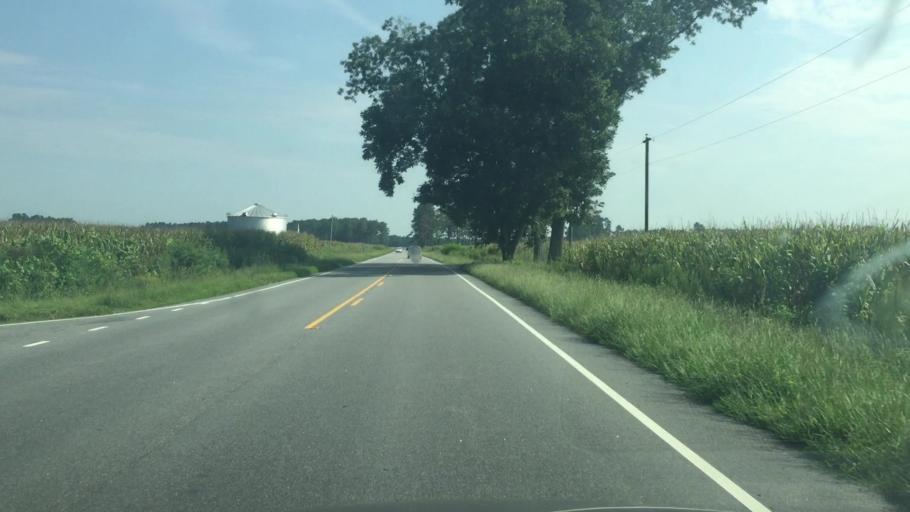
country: US
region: North Carolina
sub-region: Columbus County
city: Tabor City
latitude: 34.1695
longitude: -78.8429
